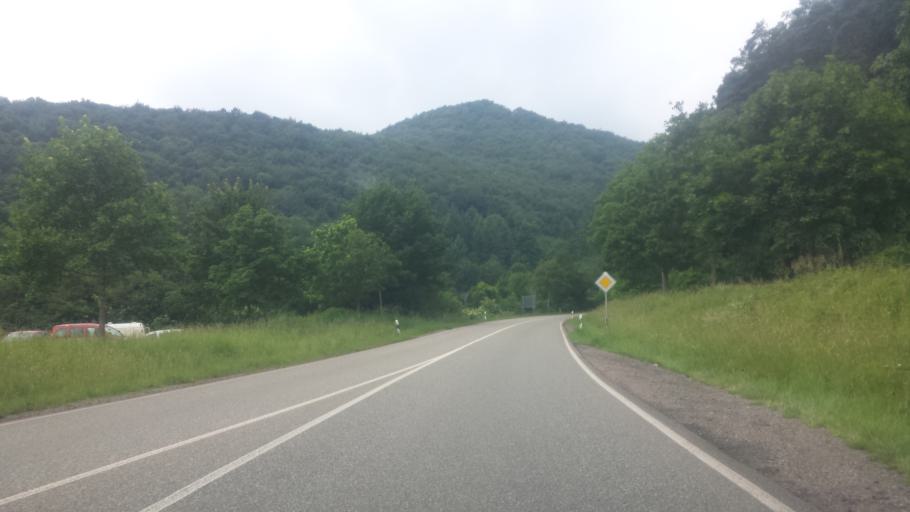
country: DE
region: Rheinland-Pfalz
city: Klingenmunster
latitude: 49.1569
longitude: 8.0126
